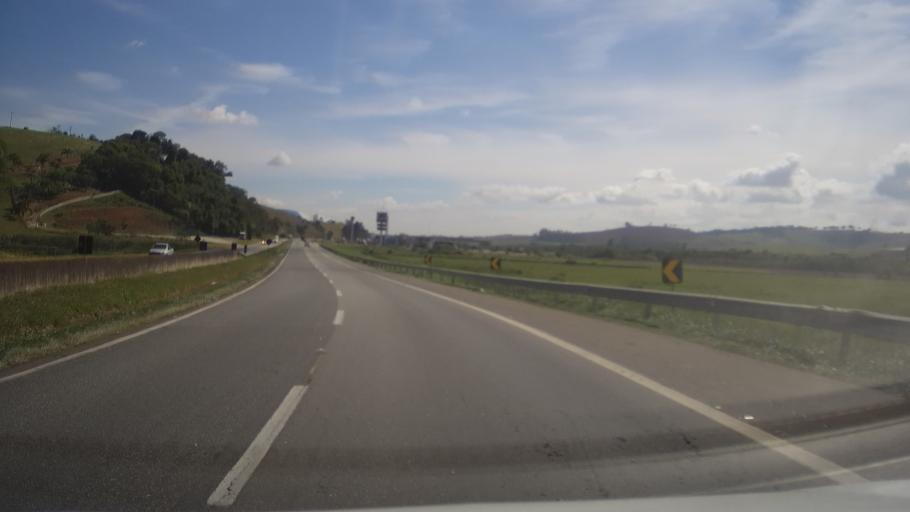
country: BR
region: Minas Gerais
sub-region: Cambui
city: Cambui
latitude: -22.5319
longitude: -46.0282
